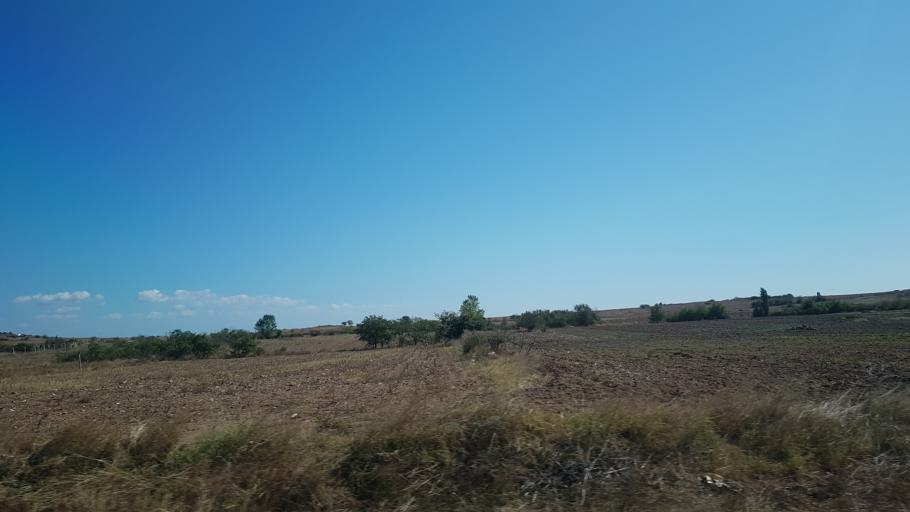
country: TR
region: Kirklareli
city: Kirklareli
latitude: 41.7654
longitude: 27.2232
